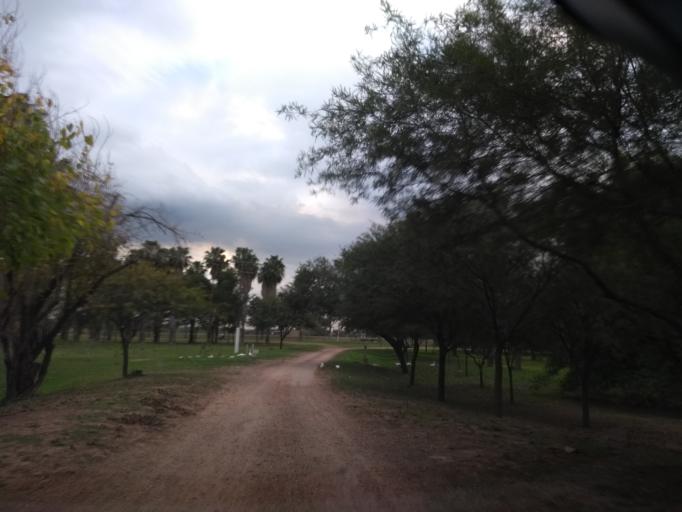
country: AR
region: Chaco
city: Presidencia Roque Saenz Pena
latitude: -26.8216
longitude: -60.4207
